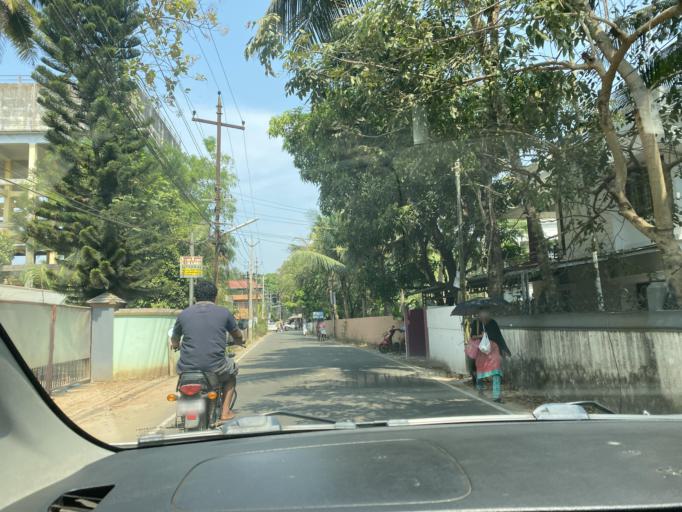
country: IN
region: Kerala
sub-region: Alappuzha
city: Arukutti
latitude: 9.9022
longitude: 76.3213
